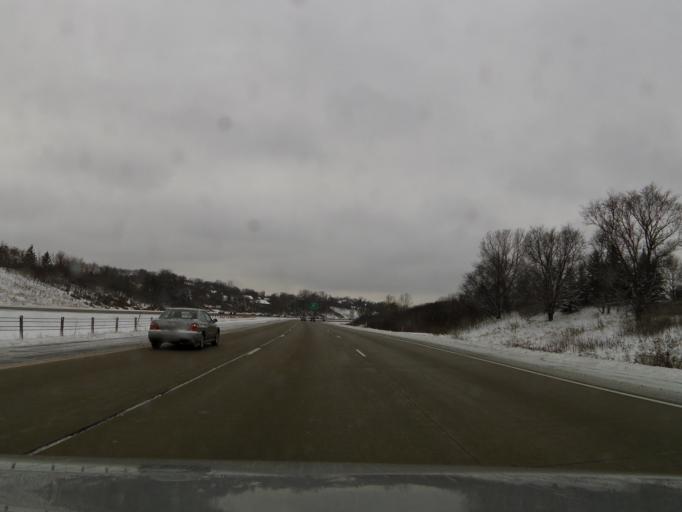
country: US
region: Minnesota
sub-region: Dakota County
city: Eagan
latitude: 44.8217
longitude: -93.1733
